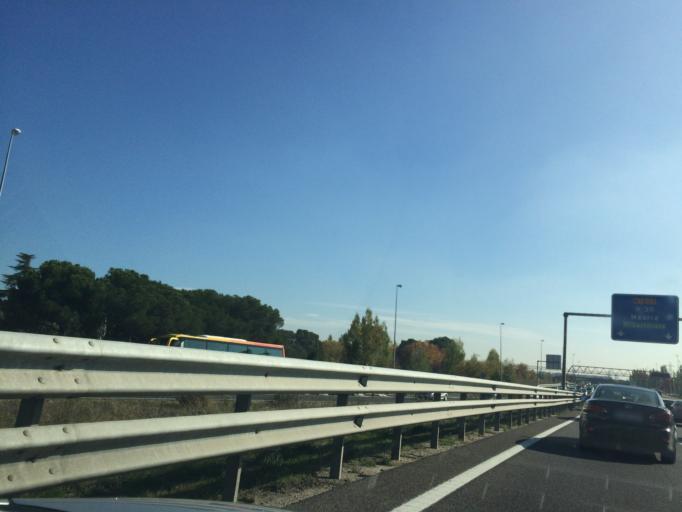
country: ES
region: Madrid
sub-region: Provincia de Madrid
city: Las Tablas
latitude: 40.5318
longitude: -3.6941
